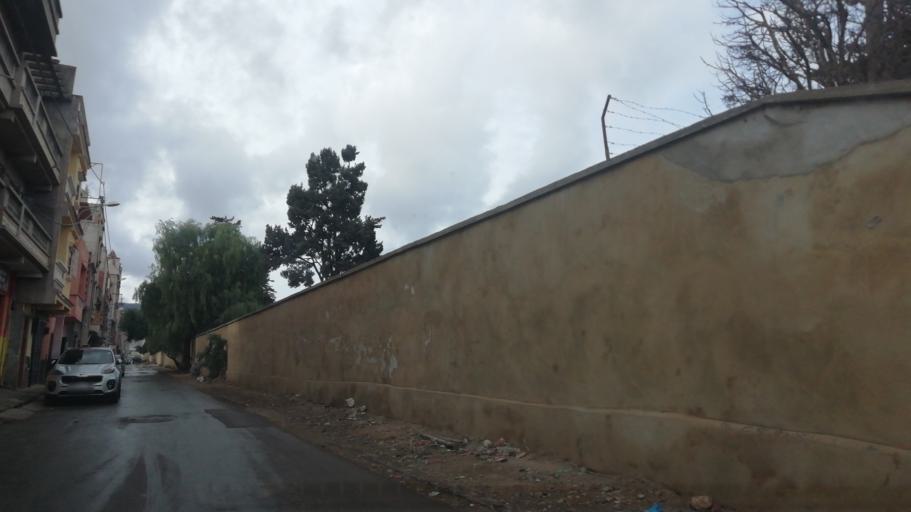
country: DZ
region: Oran
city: Oran
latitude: 35.6892
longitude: -0.6347
